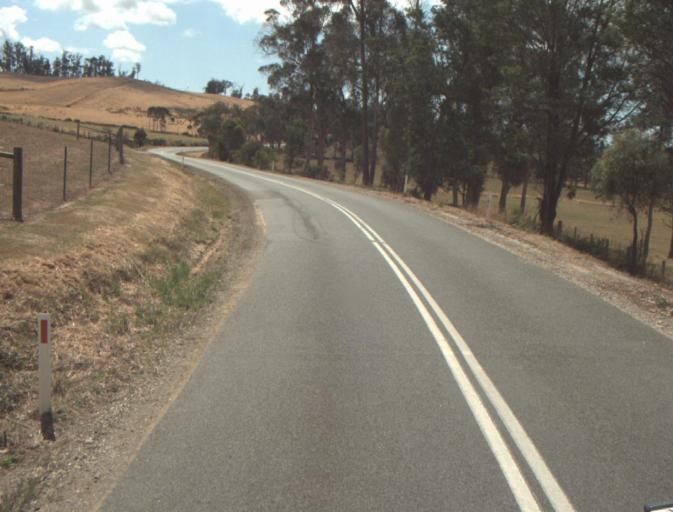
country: AU
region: Tasmania
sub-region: Launceston
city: Mayfield
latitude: -41.2255
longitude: 147.1227
